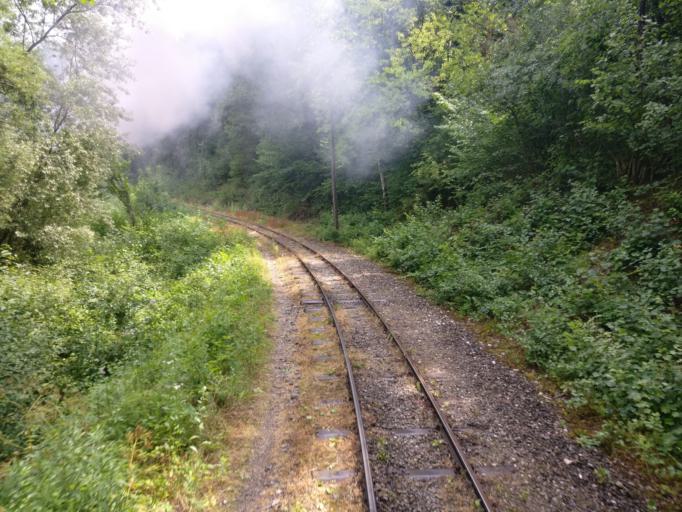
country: AT
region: Upper Austria
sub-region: Politischer Bezirk Steyr-Land
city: Sierning
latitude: 48.0439
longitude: 14.3366
